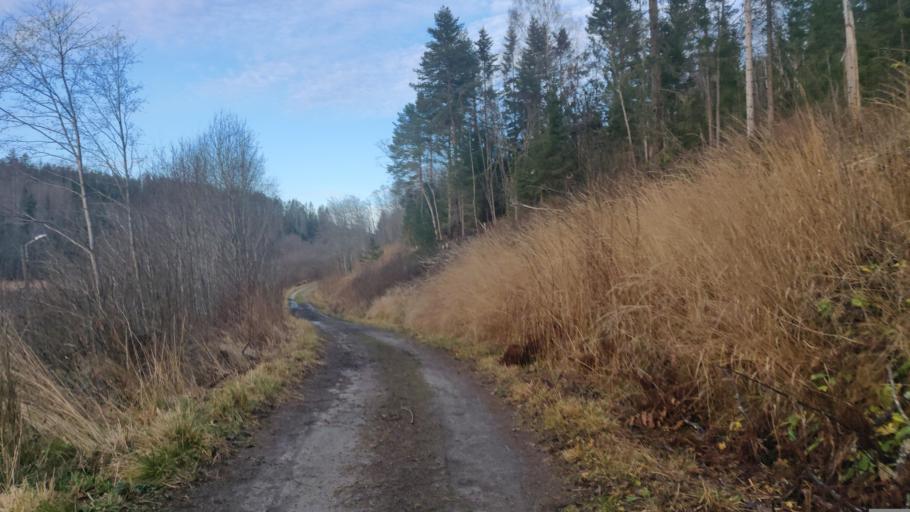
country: SE
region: Vaesternorrland
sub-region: Sundsvalls Kommun
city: Nolby
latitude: 62.2992
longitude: 17.3582
